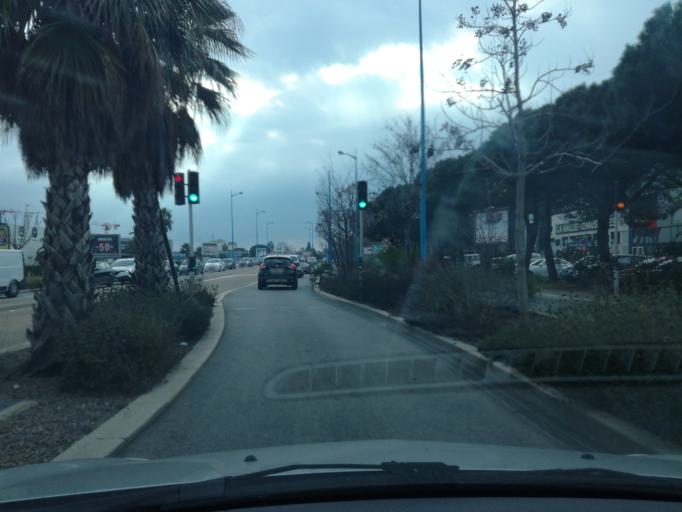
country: FR
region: Provence-Alpes-Cote d'Azur
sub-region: Departement des Alpes-Maritimes
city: Mandelieu-la-Napoule
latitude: 43.5545
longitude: 6.9543
